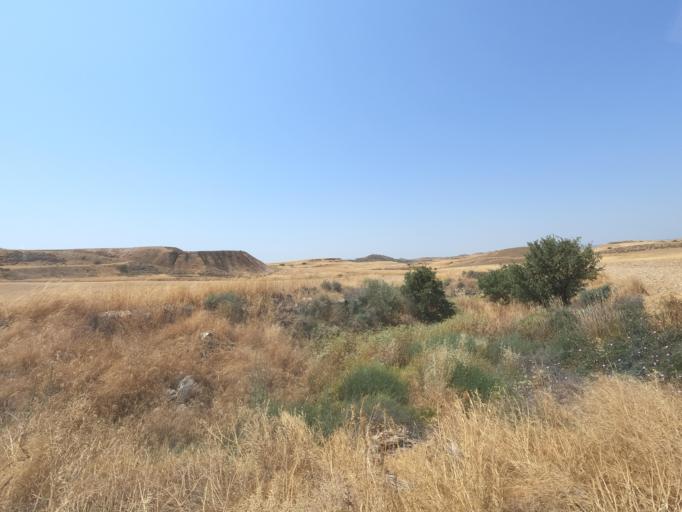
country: CY
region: Larnaka
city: Troulloi
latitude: 35.0311
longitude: 33.6395
